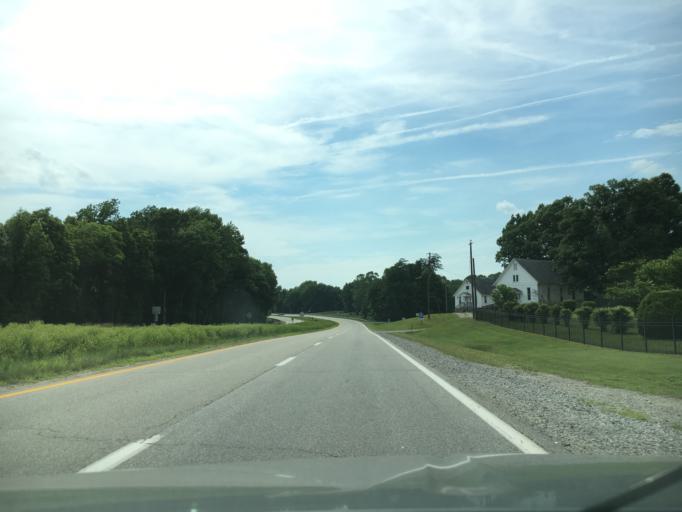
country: US
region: Virginia
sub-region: Prince Edward County
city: Hampden Sydney
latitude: 37.1054
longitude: -78.3628
